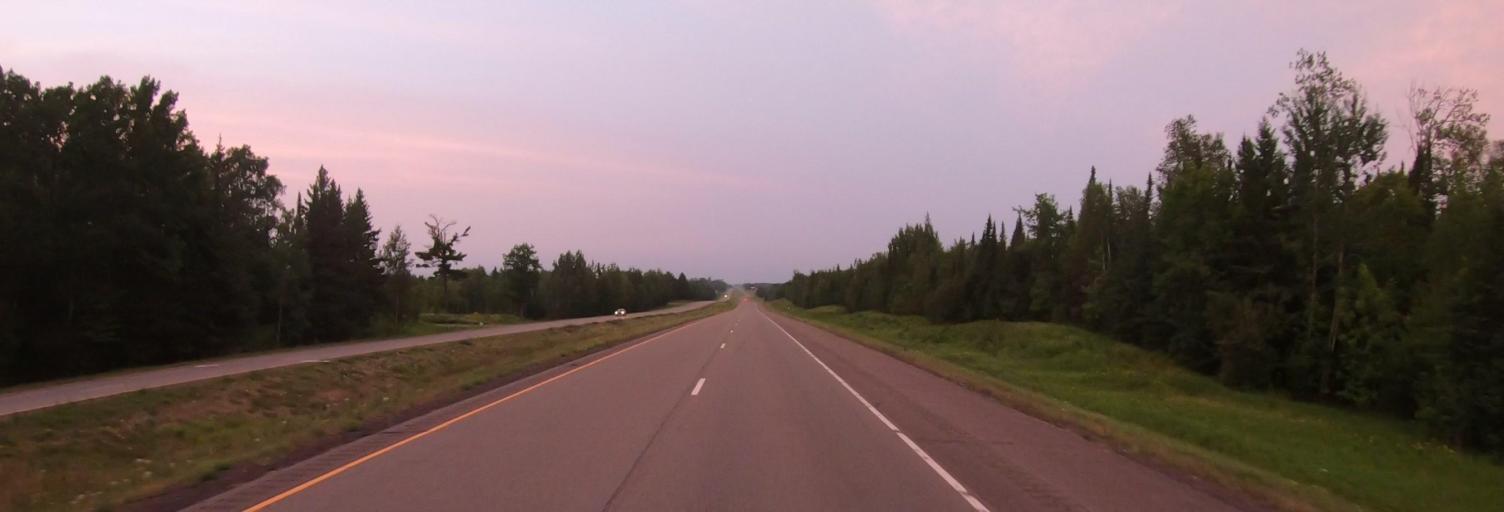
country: US
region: Minnesota
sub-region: Carlton County
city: Cloquet
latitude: 47.0148
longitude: -92.4709
